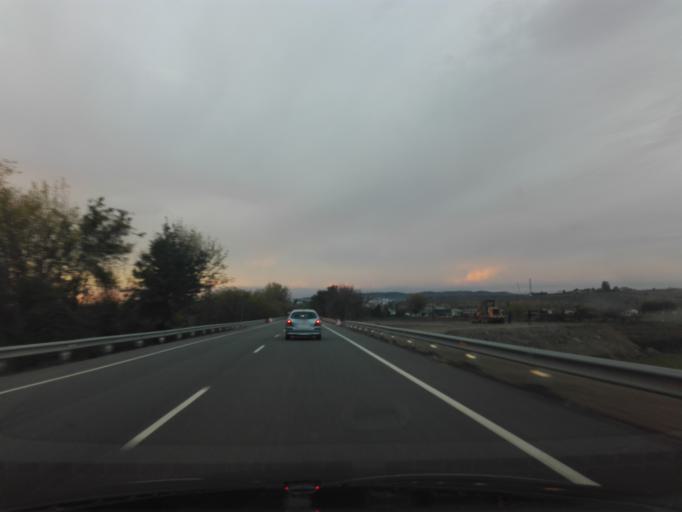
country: ES
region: Extremadura
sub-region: Provincia de Caceres
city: Coria
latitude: 39.9704
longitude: -6.5224
